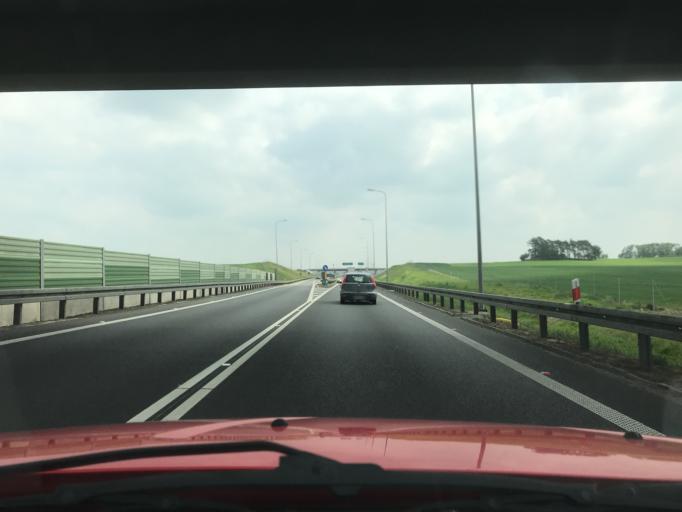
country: PL
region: Greater Poland Voivodeship
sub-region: Powiat sredzki
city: Nowe Miasto nad Warta
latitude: 52.0405
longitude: 17.4625
